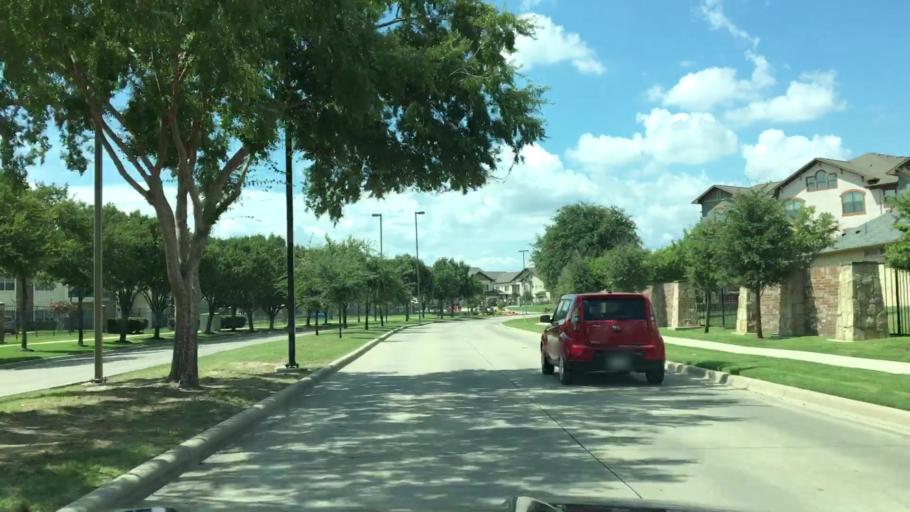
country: US
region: Texas
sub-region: Tarrant County
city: Keller
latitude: 32.9392
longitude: -97.2416
